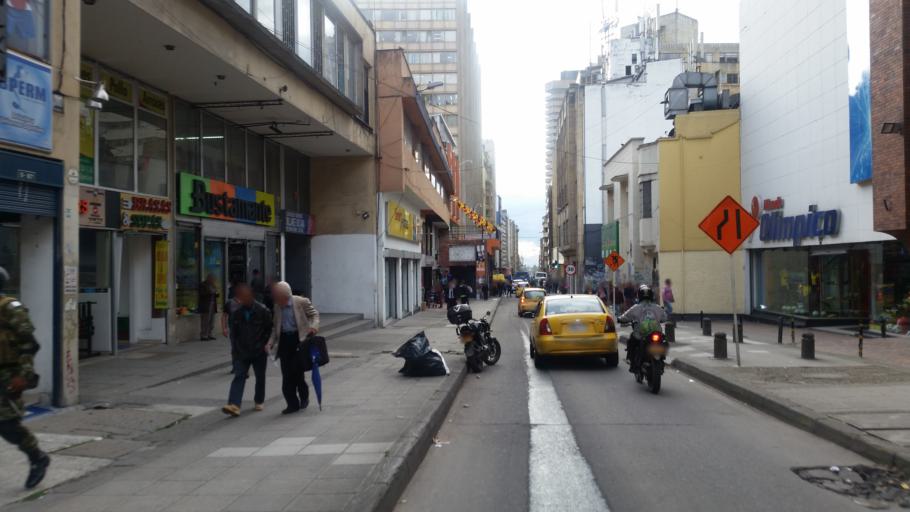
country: CO
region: Bogota D.C.
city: Bogota
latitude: 4.6030
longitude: -74.0716
